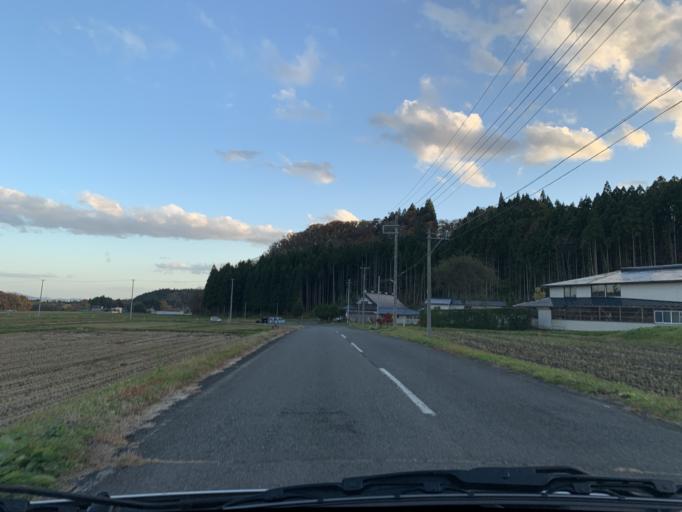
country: JP
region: Iwate
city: Mizusawa
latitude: 39.0411
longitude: 141.0513
